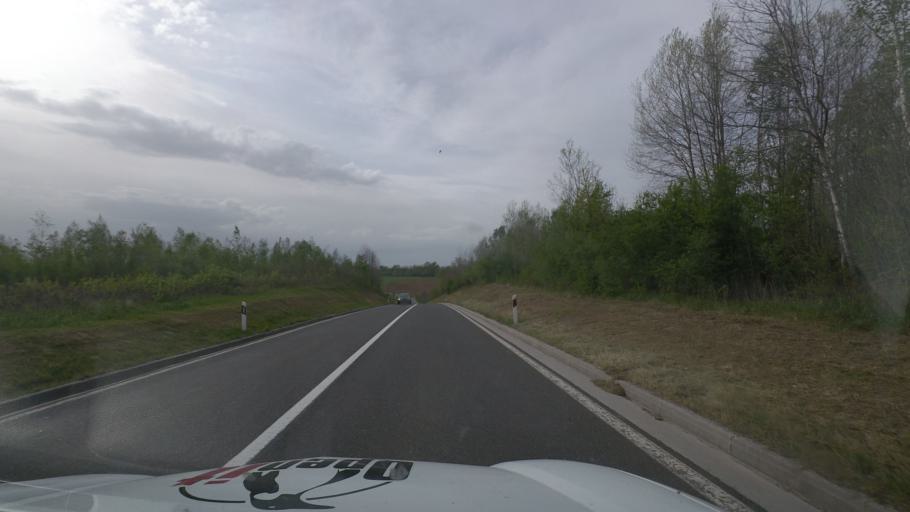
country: HR
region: Sisacko-Moslavacka
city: Gvozd
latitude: 45.3267
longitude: 15.9389
